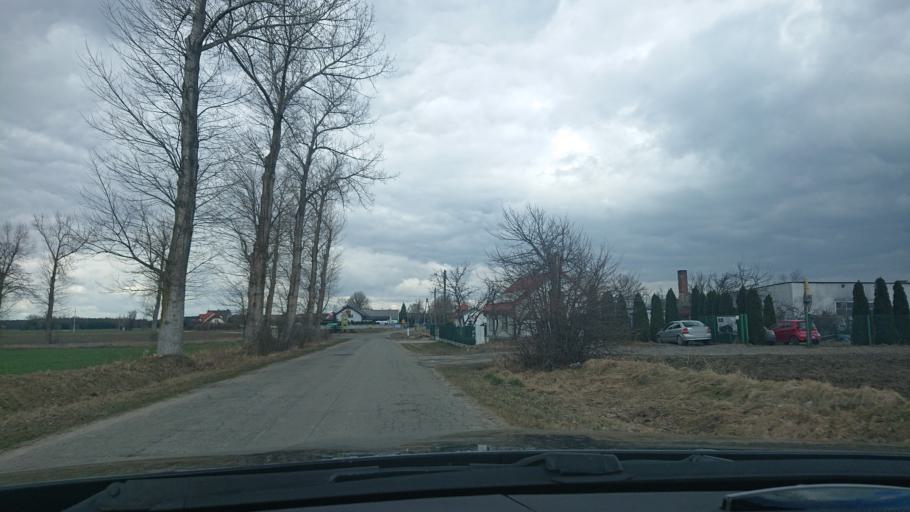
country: PL
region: Greater Poland Voivodeship
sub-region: Powiat gnieznienski
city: Niechanowo
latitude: 52.5877
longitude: 17.6990
